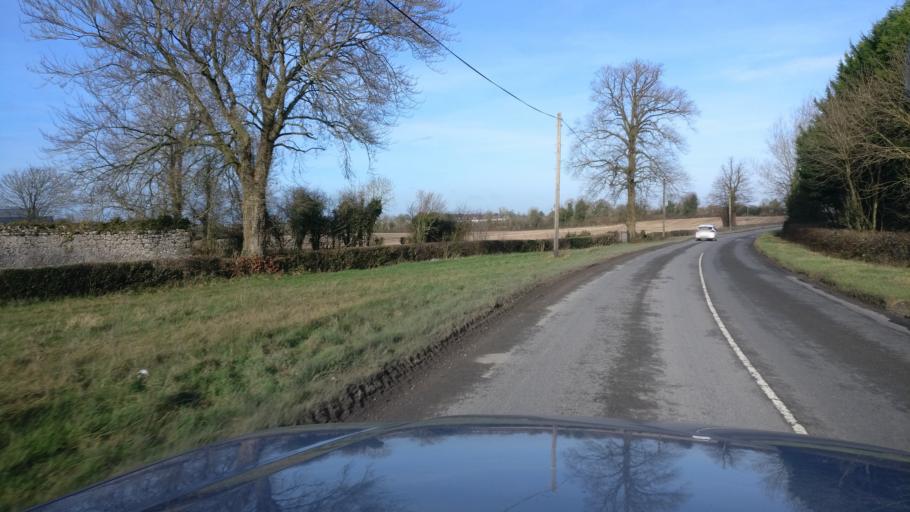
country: IE
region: Leinster
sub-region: Laois
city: Portlaoise
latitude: 53.0206
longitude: -7.2733
